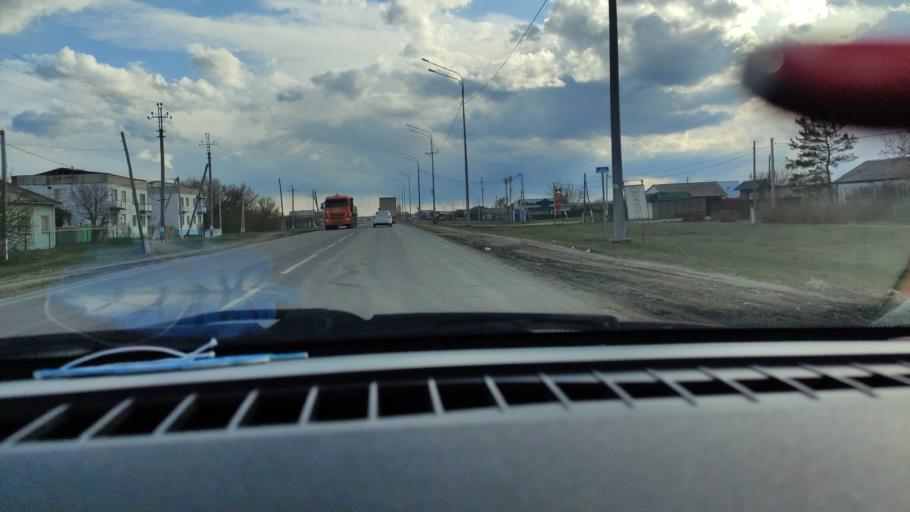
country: RU
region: Saratov
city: Sinodskoye
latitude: 51.9878
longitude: 46.6654
